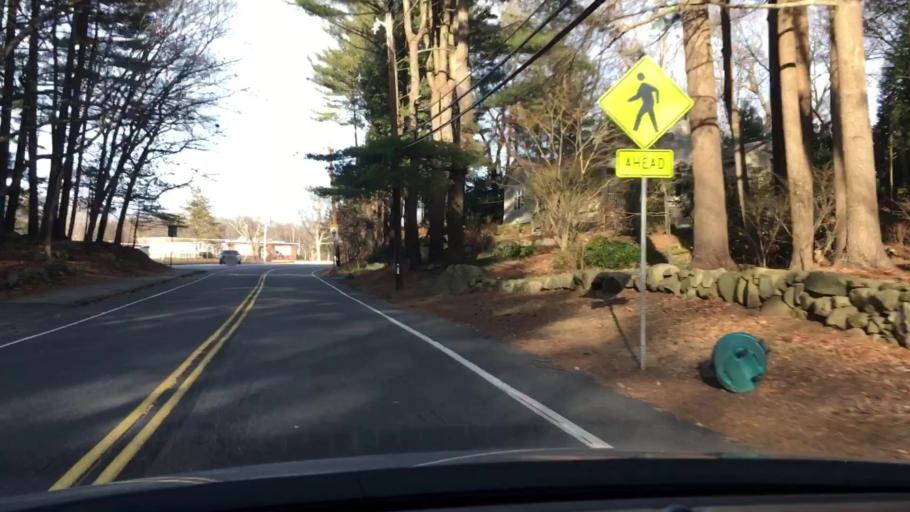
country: US
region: Massachusetts
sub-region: Norfolk County
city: Norwood
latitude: 42.2244
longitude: -71.1922
